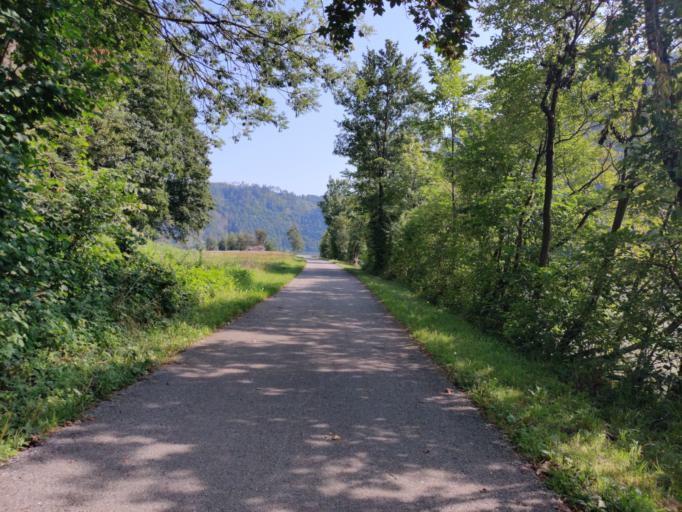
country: AT
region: Upper Austria
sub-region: Politischer Bezirk Rohrbach
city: Kleinzell im Muehlkreis
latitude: 48.4071
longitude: 13.9485
